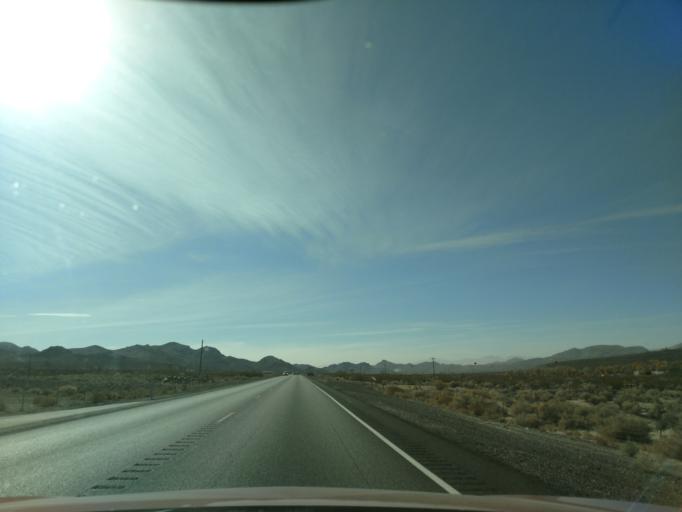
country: US
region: Nevada
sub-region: Nye County
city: Beatty
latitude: 36.9440
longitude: -116.7194
